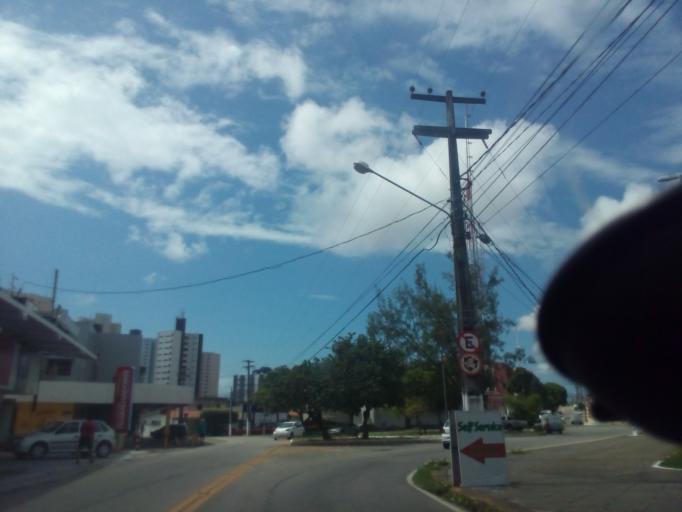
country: BR
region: Rio Grande do Norte
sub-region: Natal
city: Natal
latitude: -5.8389
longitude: -35.2169
